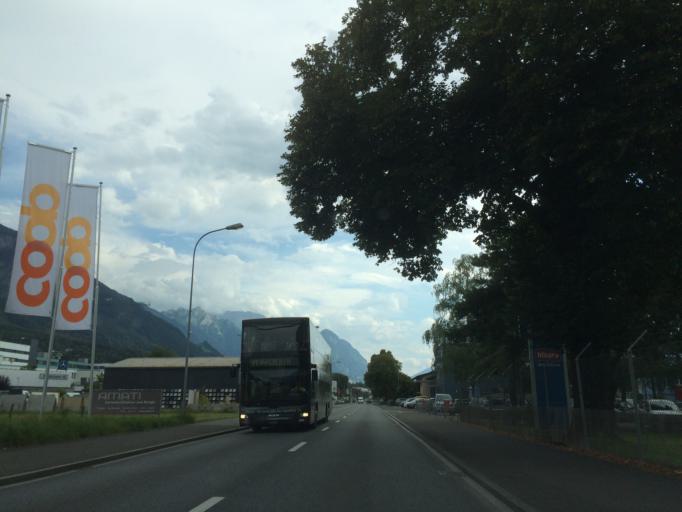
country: LI
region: Schaan
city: Schaan
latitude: 47.1754
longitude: 9.5086
